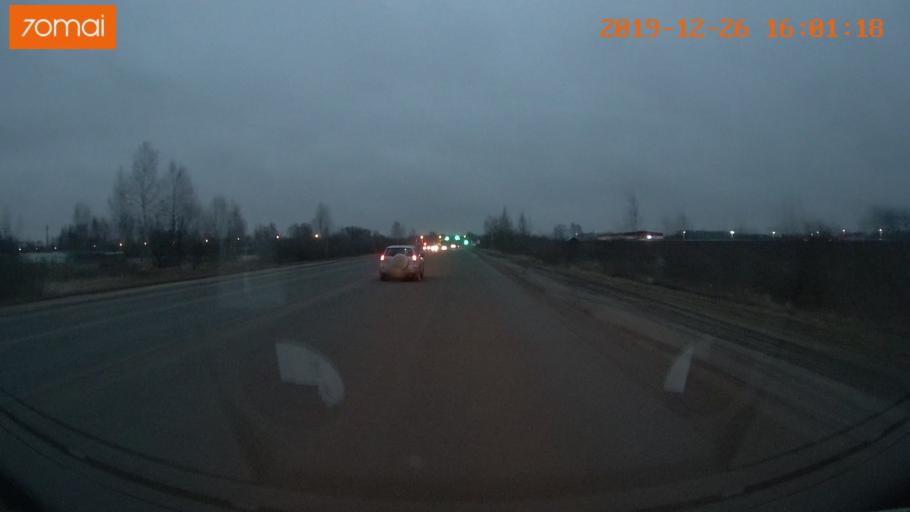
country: RU
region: Jaroslavl
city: Rybinsk
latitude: 58.0168
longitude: 38.8177
